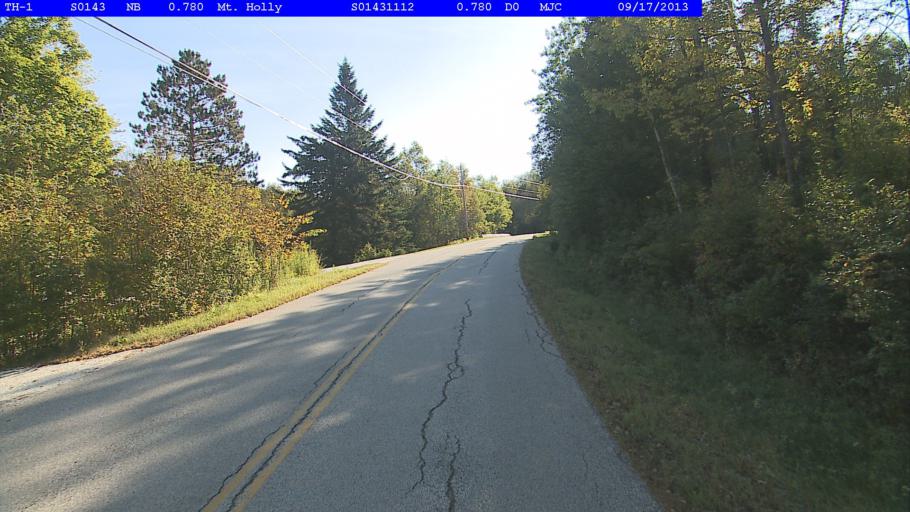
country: US
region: Vermont
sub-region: Rutland County
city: Rutland
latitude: 43.4137
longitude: -72.8270
